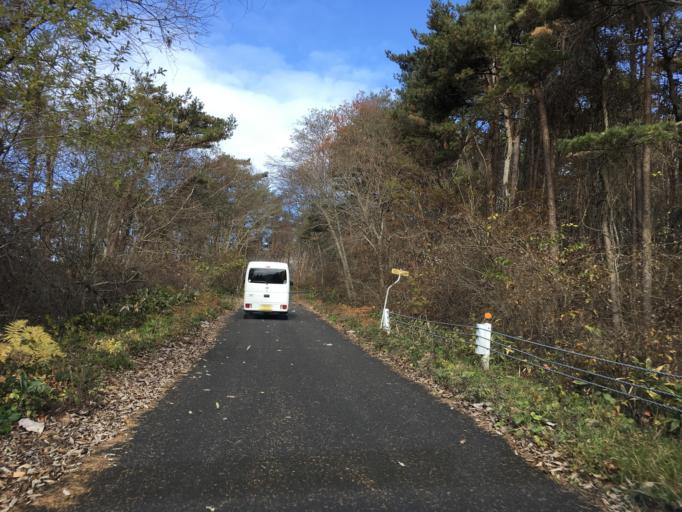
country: JP
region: Iwate
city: Mizusawa
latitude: 39.1309
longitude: 141.3024
